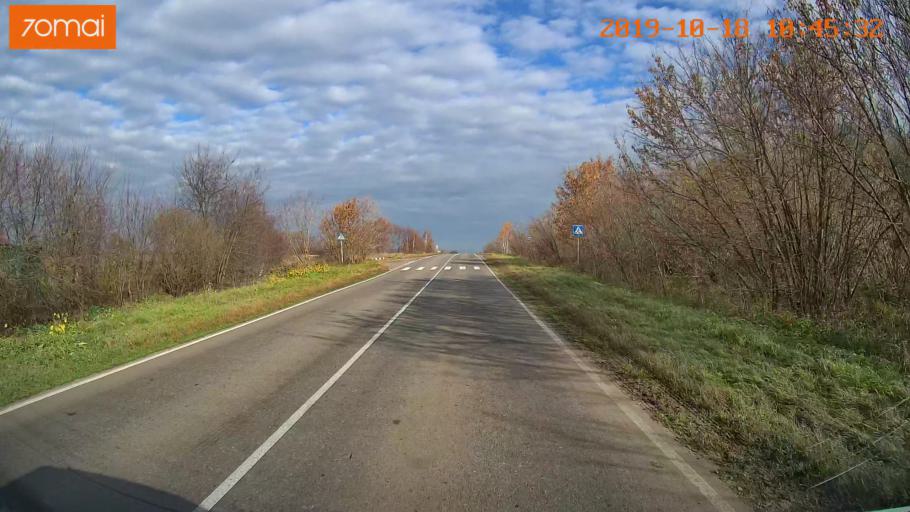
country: RU
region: Tula
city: Yepifan'
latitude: 53.6716
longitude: 38.6892
